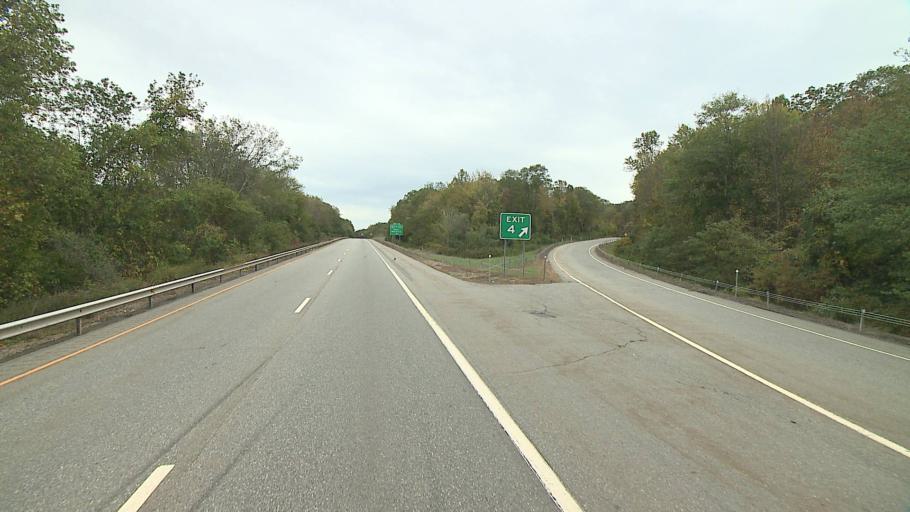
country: US
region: Connecticut
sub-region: Middlesex County
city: Deep River Center
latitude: 41.3631
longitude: -72.4269
